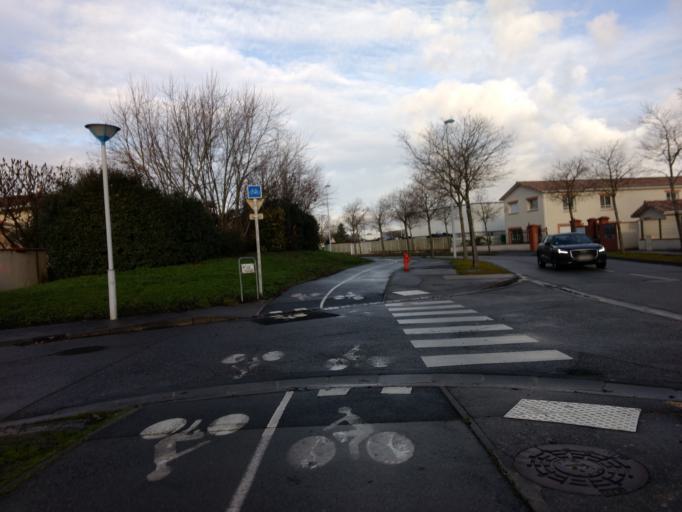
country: FR
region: Midi-Pyrenees
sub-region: Departement de la Haute-Garonne
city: Tournefeuille
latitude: 43.6017
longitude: 1.3204
